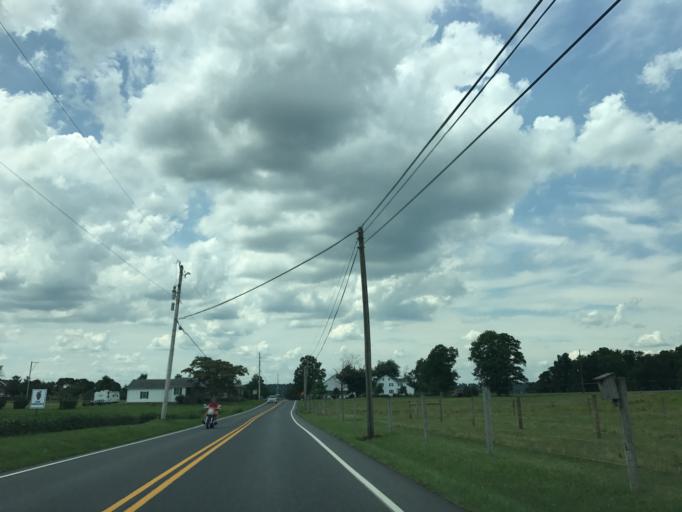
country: US
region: Pennsylvania
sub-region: Lancaster County
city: Mount Joy
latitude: 40.1835
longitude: -76.5023
